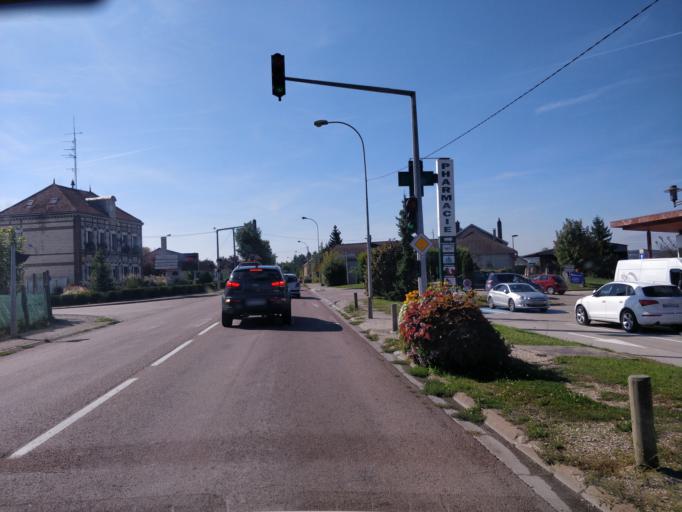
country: FR
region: Champagne-Ardenne
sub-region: Departement de l'Aube
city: Saint-Germain
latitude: 48.2572
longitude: 4.0302
